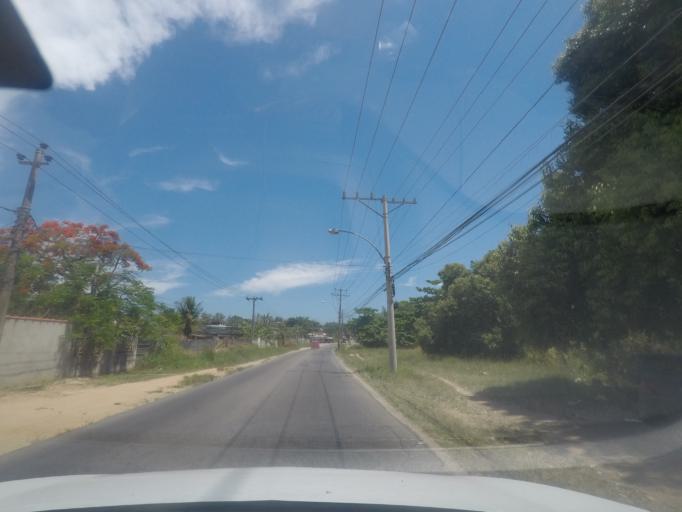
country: BR
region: Rio de Janeiro
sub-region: Itaguai
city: Itaguai
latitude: -22.9922
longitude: -43.6509
